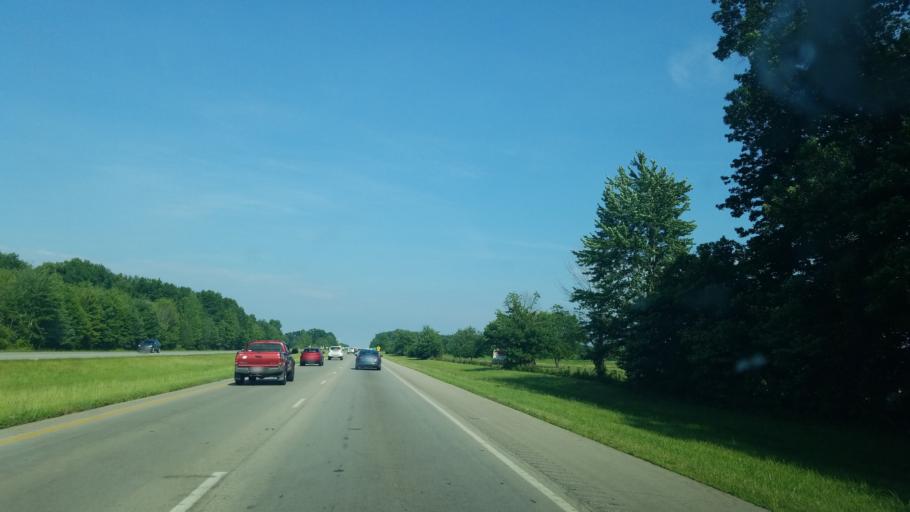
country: US
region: Ohio
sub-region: Clermont County
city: Batavia
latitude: 39.0810
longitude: -84.1420
